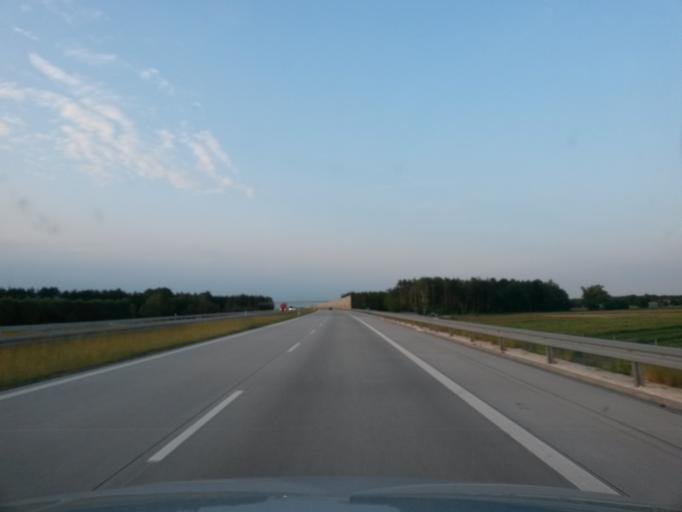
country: PL
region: Lodz Voivodeship
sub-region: Powiat wieruszowski
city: Lututow
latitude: 51.3419
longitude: 18.4990
